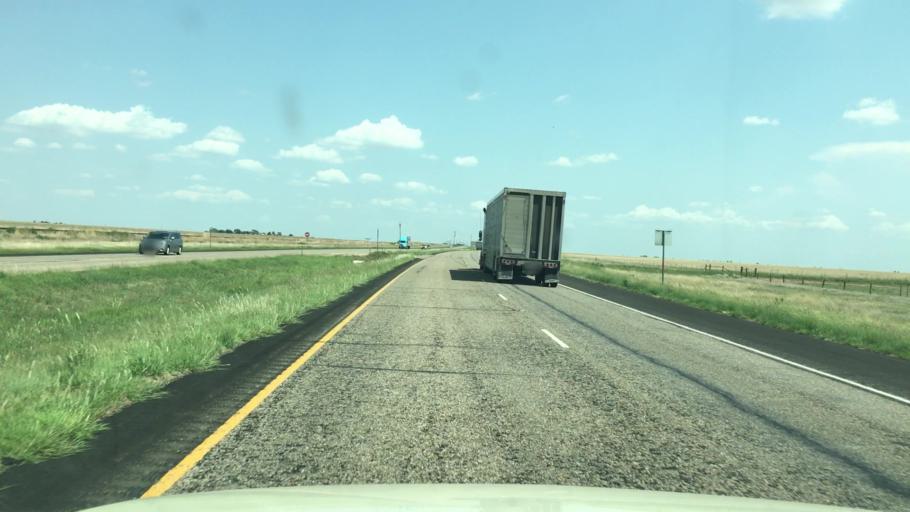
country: US
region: Texas
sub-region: Armstrong County
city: Claude
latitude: 35.1265
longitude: -101.4001
